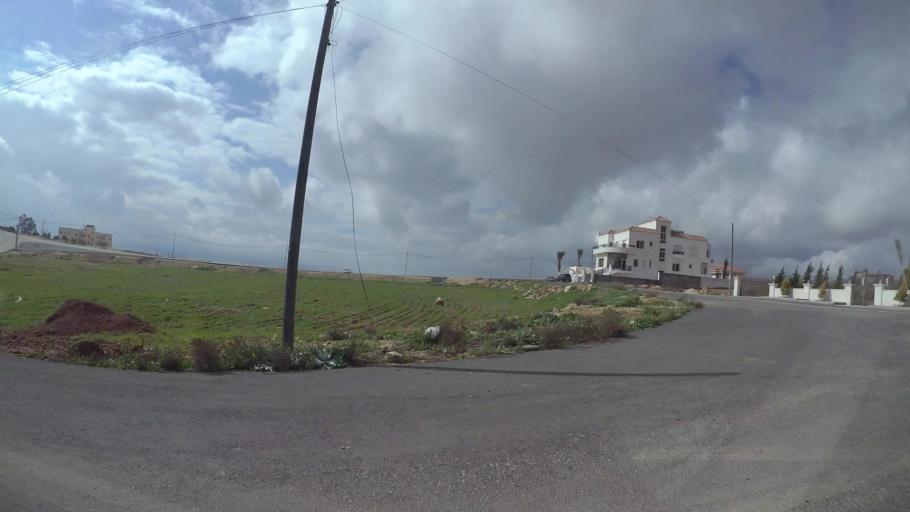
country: JO
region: Amman
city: Al Jubayhah
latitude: 32.0764
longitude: 35.8845
